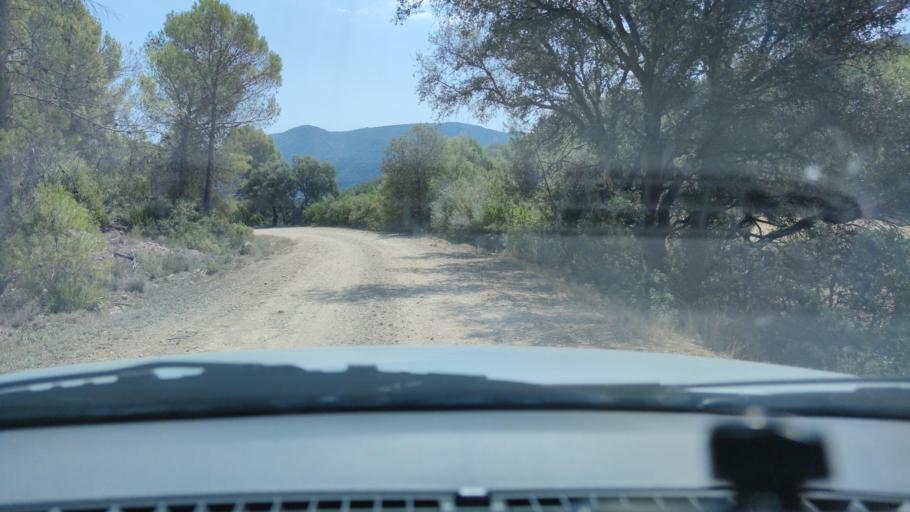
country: ES
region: Catalonia
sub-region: Provincia de Lleida
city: Camarasa
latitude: 41.9244
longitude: 0.8438
